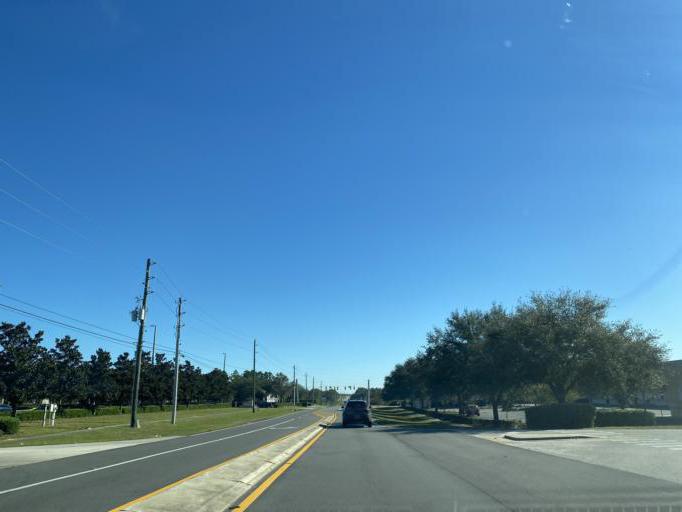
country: US
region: Florida
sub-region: Lake County
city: Clermont
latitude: 28.4998
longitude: -81.7175
